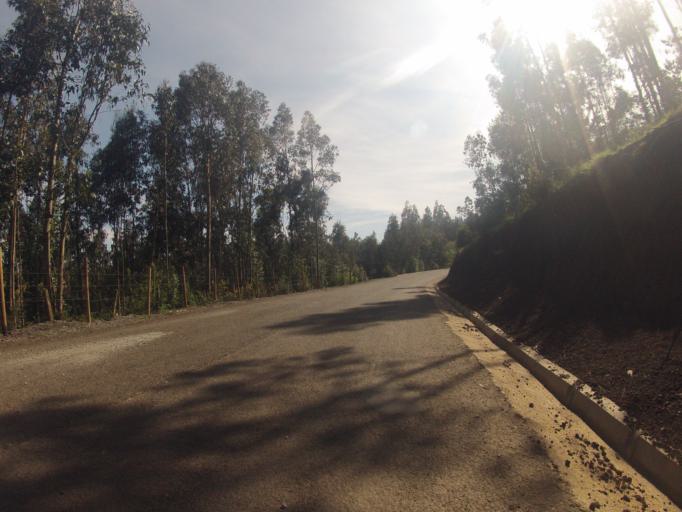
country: CL
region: Araucania
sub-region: Provincia de Cautin
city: Temuco
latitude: -38.7019
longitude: -72.5940
